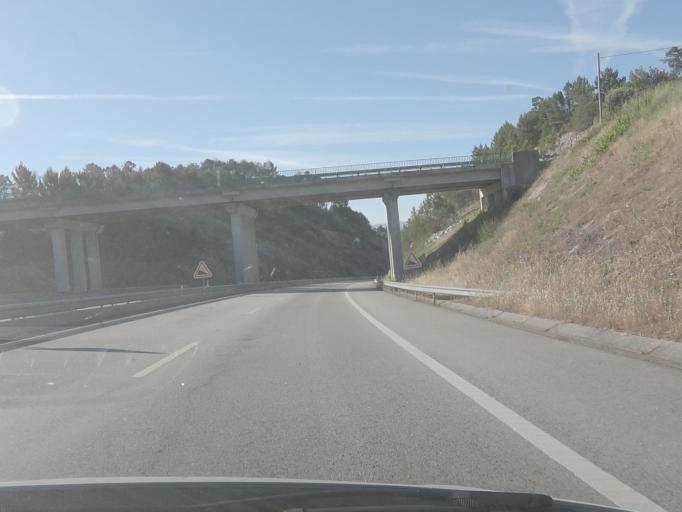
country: PT
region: Viseu
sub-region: Viseu
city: Campo
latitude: 40.7763
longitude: -7.9270
